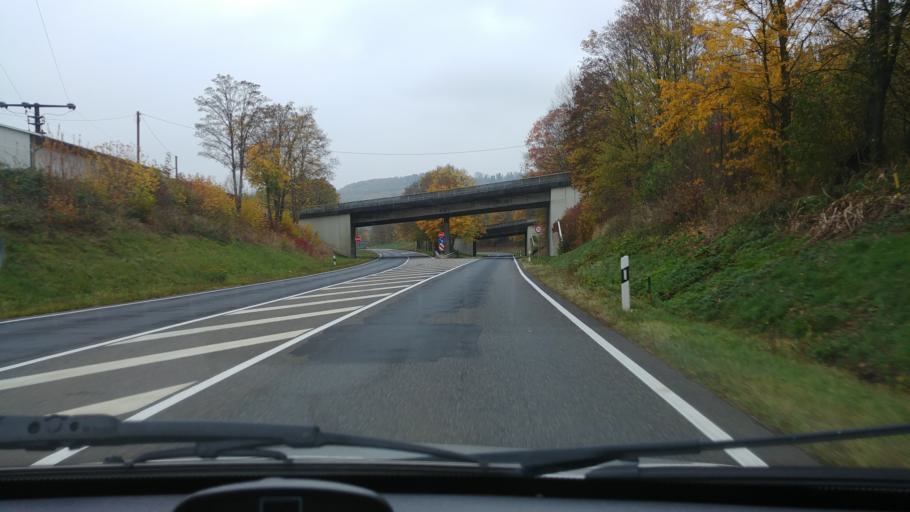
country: DE
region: Rheinland-Pfalz
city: Nauroth
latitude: 50.6693
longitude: 7.8646
